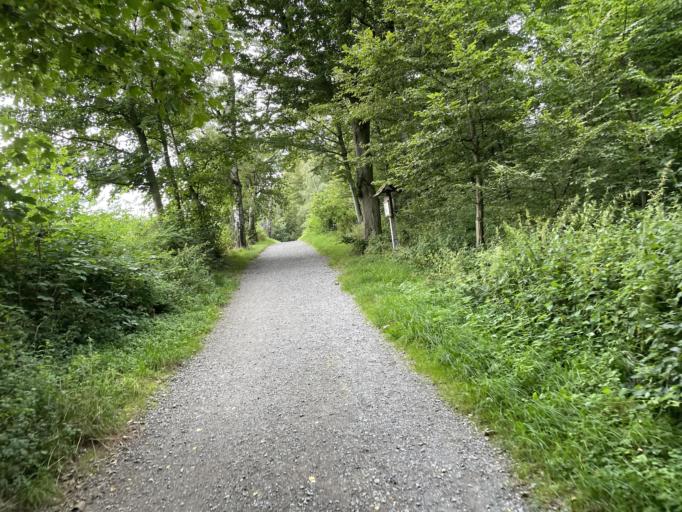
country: DE
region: North Rhine-Westphalia
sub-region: Regierungsbezirk Dusseldorf
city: Heiligenhaus
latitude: 51.3741
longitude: 6.9554
